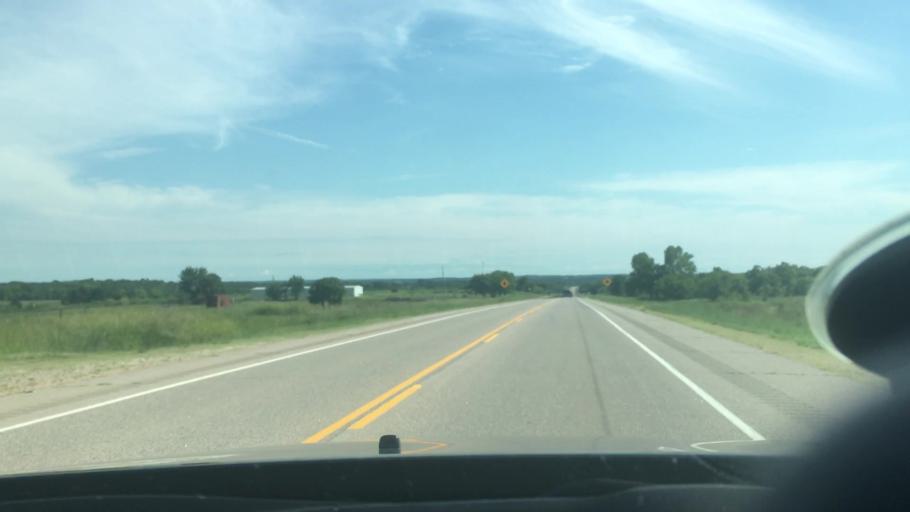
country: US
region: Oklahoma
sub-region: Seminole County
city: Maud
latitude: 35.0900
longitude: -96.6788
